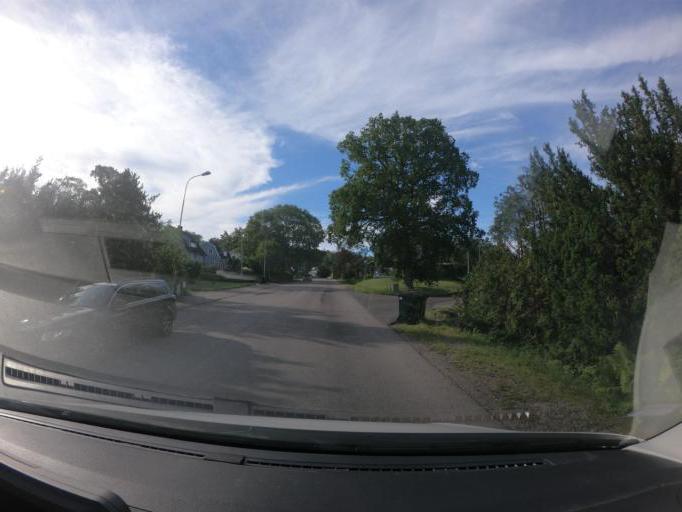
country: SE
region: Skane
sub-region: Orkelljunga Kommun
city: OErkelljunga
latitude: 56.2744
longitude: 13.2870
